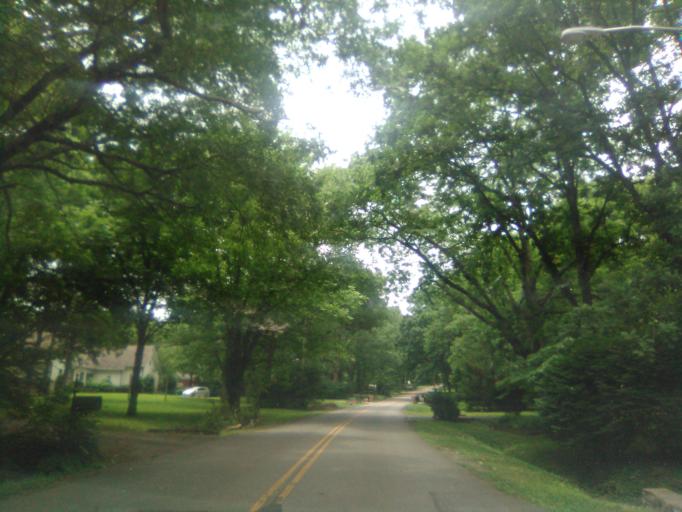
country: US
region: Tennessee
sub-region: Davidson County
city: Belle Meade
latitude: 36.1098
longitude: -86.8769
